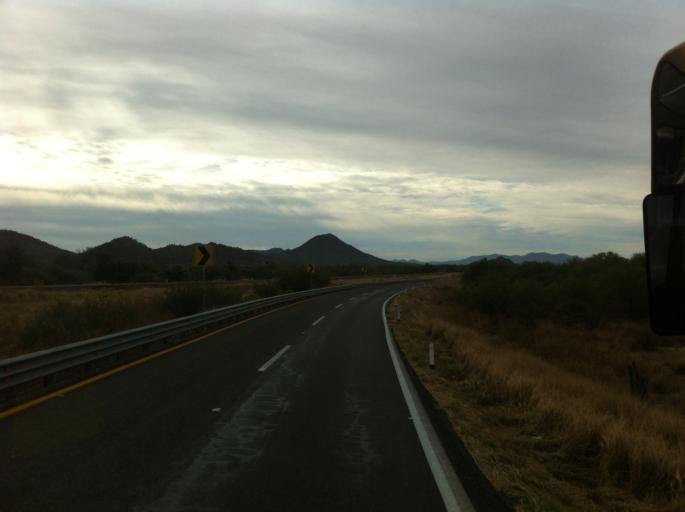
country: MX
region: Sonora
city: Hermosillo
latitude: 28.8662
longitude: -110.9592
